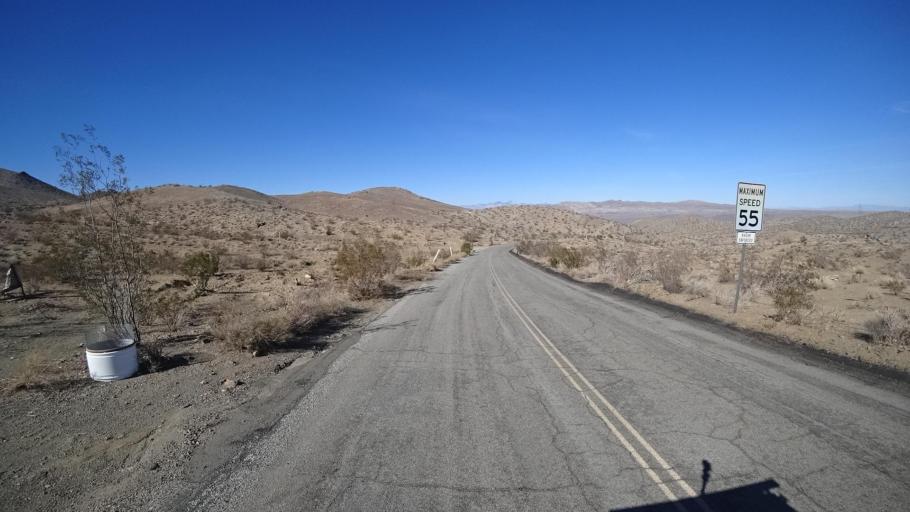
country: US
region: California
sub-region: Kern County
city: Ridgecrest
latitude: 35.3691
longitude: -117.6589
